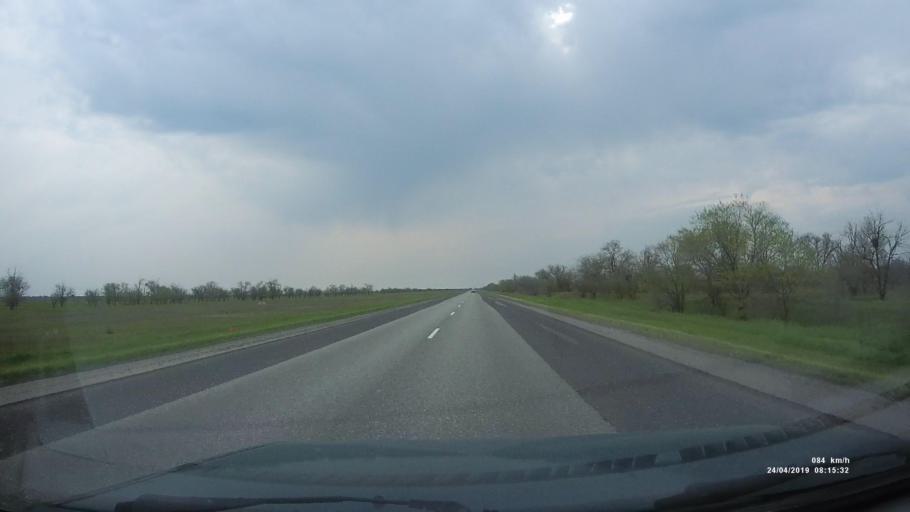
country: RU
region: Kalmykiya
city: Priyutnoye
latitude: 46.1001
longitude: 43.5968
